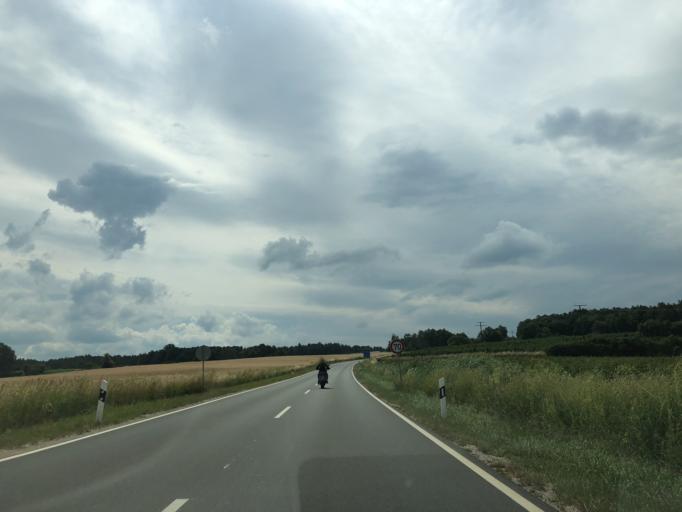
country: DE
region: Bavaria
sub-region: Regierungsbezirk Mittelfranken
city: Muhlhausen
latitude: 49.7424
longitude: 10.7863
